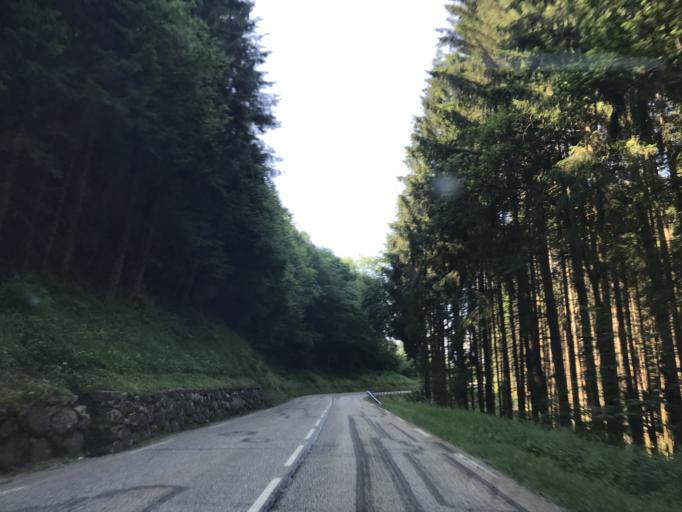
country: FR
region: Rhone-Alpes
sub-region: Departement de l'Isere
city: Allevard
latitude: 45.3289
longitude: 6.0916
